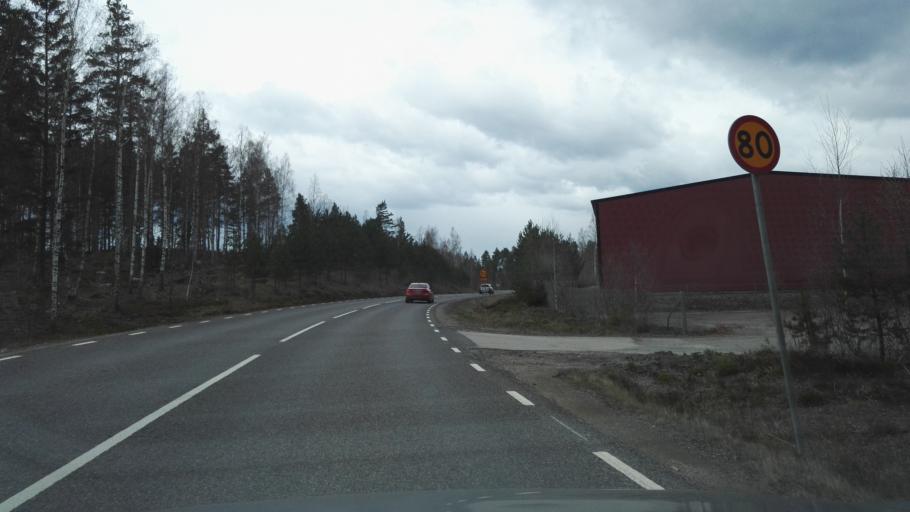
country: SE
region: Kronoberg
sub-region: Vaxjo Kommun
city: Braas
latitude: 57.0559
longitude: 15.0389
